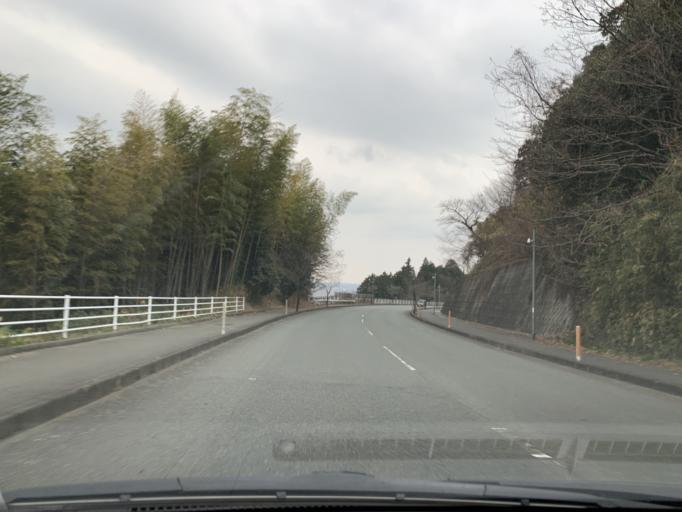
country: JP
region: Kumamoto
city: Ozu
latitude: 32.8830
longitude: 130.8818
